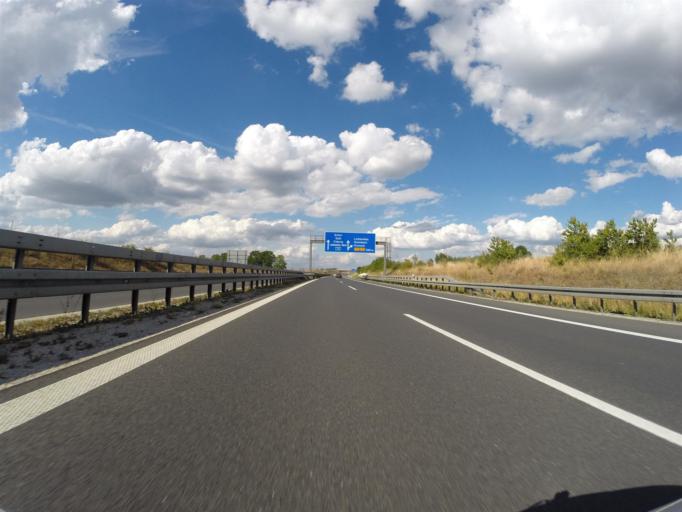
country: DE
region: Bavaria
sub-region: Upper Franconia
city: Bad Staffelstein
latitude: 50.1198
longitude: 11.0218
